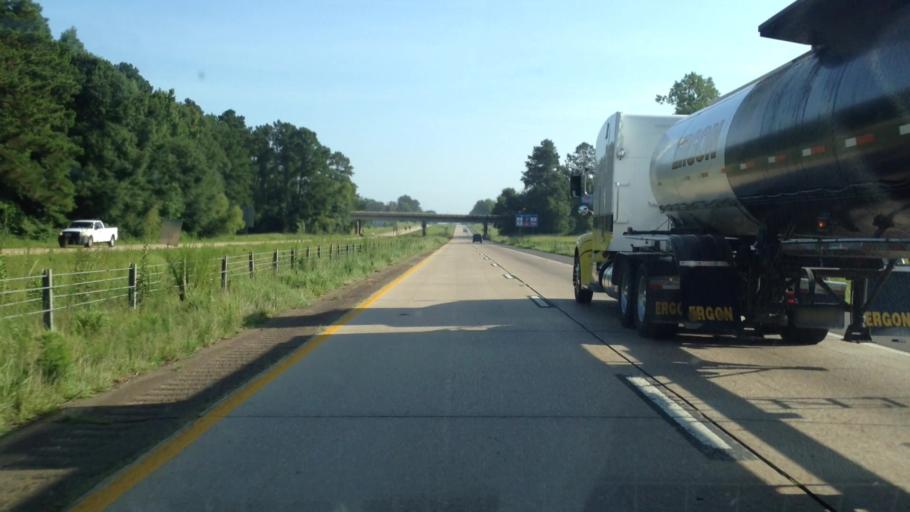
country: US
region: Mississippi
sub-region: Pike County
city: McComb
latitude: 31.2351
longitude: -90.4813
